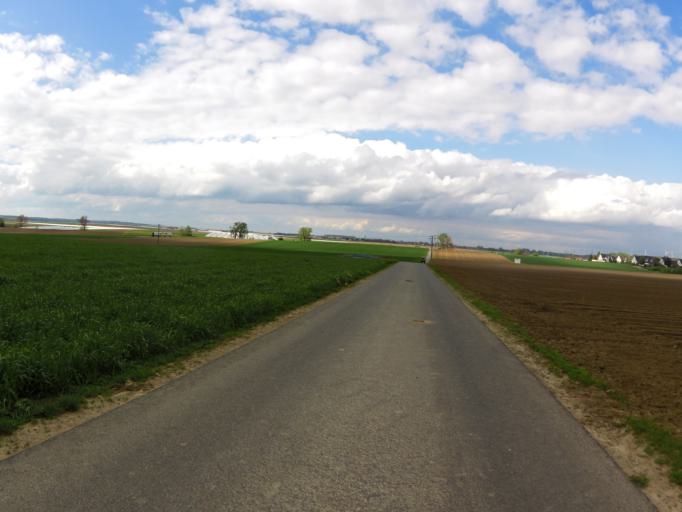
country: DE
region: Bavaria
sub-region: Regierungsbezirk Unterfranken
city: Oberpleichfeld
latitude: 49.8714
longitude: 10.0798
